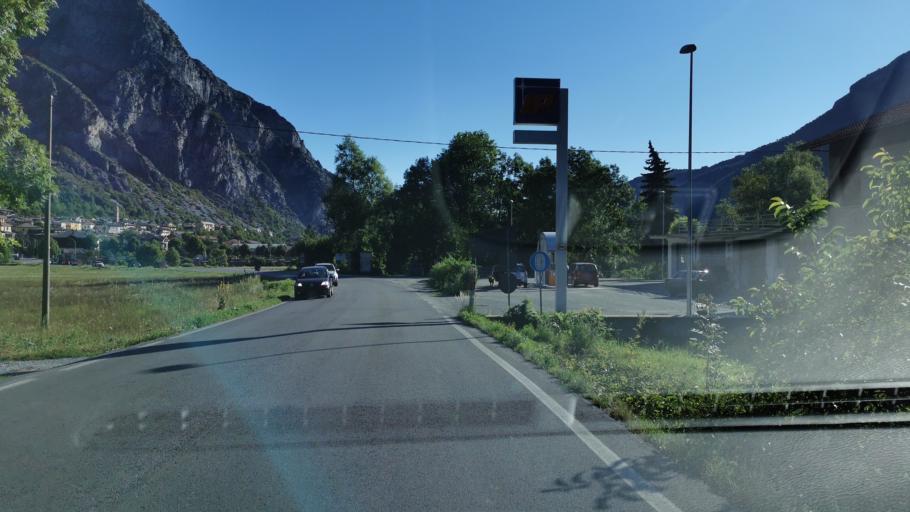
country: IT
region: Piedmont
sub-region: Provincia di Cuneo
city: Valdieri
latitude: 44.2721
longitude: 7.3954
